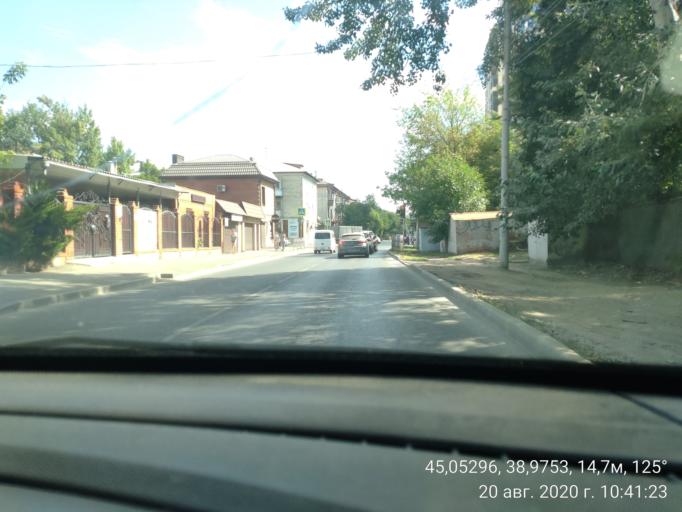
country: RU
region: Krasnodarskiy
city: Krasnodar
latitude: 45.0529
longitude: 38.9752
